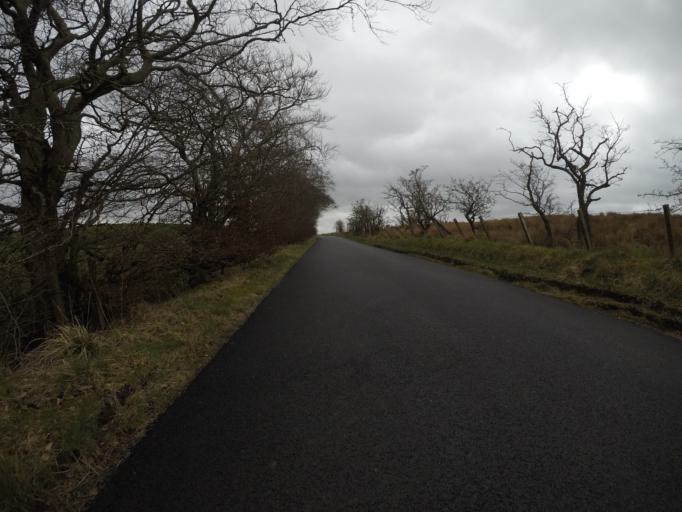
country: GB
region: Scotland
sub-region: East Ayrshire
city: Stewarton
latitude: 55.6817
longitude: -4.4599
